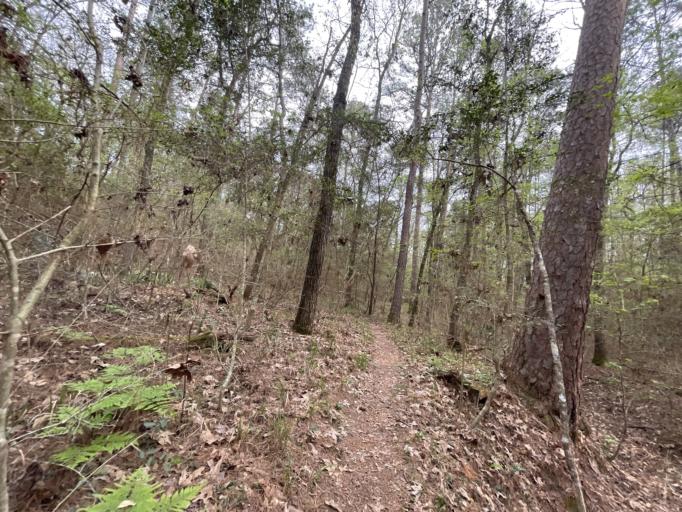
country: US
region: Texas
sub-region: Walker County
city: Huntsville
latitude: 30.6576
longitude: -95.4845
